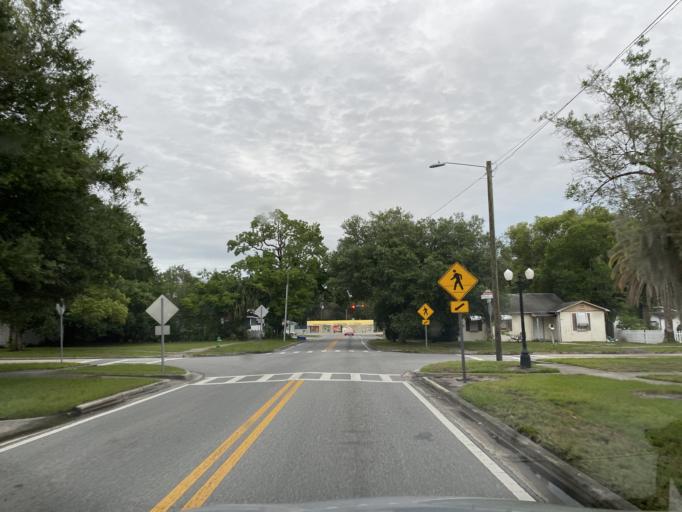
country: US
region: Florida
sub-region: Seminole County
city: Sanford
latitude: 28.8008
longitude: -81.2662
